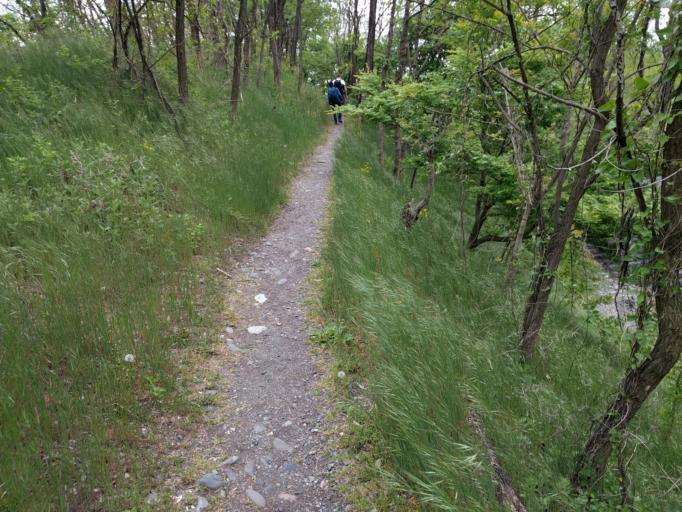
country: JP
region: Nagano
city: Hotaka
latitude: 36.3365
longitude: 137.9124
